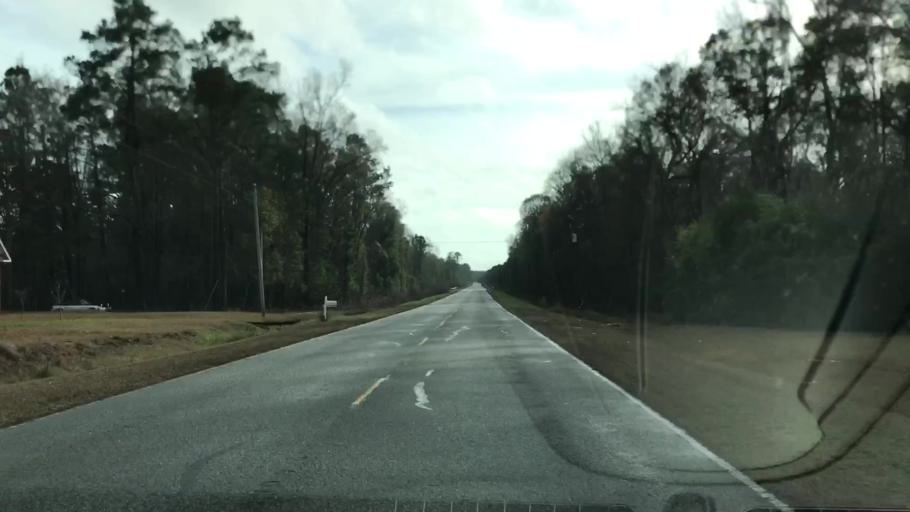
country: US
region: South Carolina
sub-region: Williamsburg County
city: Andrews
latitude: 33.4349
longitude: -79.5928
